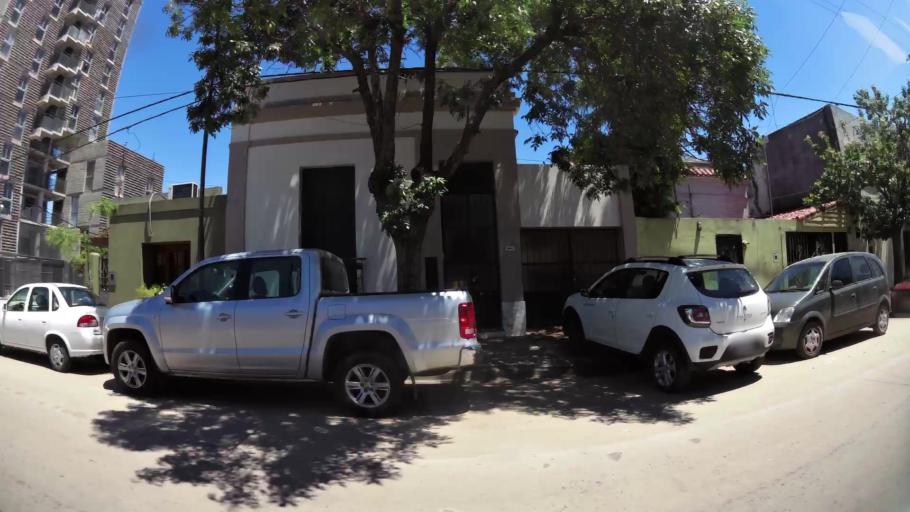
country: AR
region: Santa Fe
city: Santa Fe de la Vera Cruz
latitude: -31.6321
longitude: -60.7093
